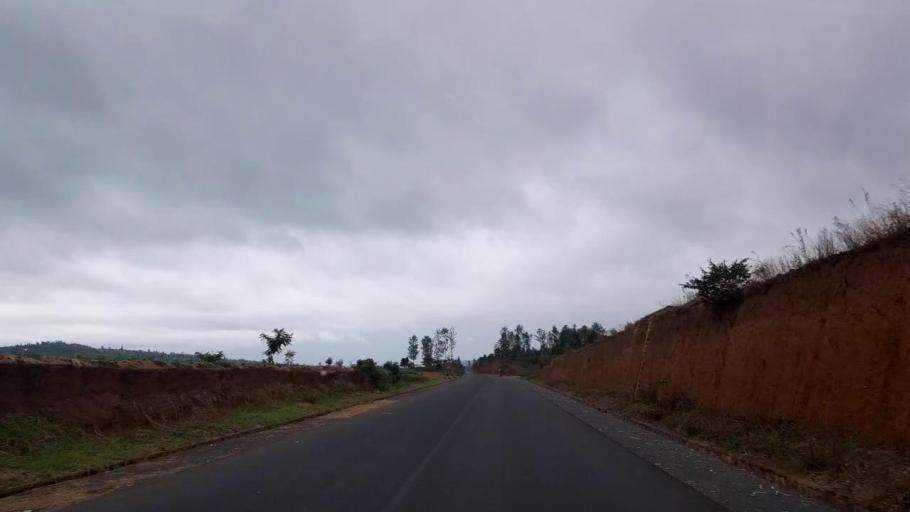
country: RW
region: Northern Province
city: Byumba
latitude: -1.4337
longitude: 30.2607
